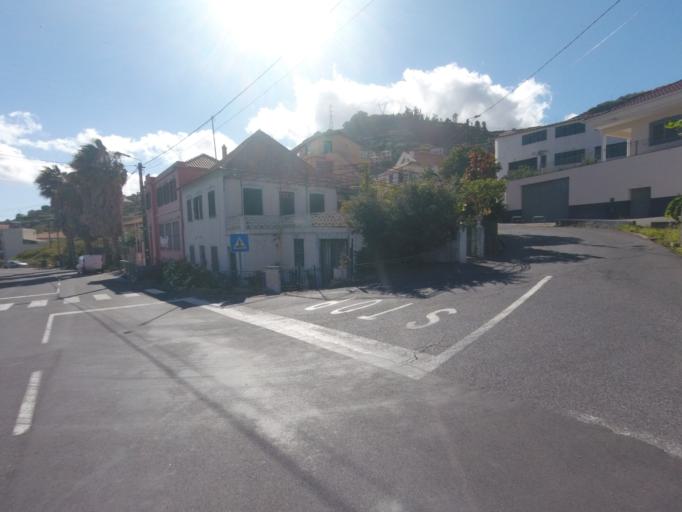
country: PT
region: Madeira
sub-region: Ribeira Brava
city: Campanario
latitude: 32.6733
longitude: -17.0283
